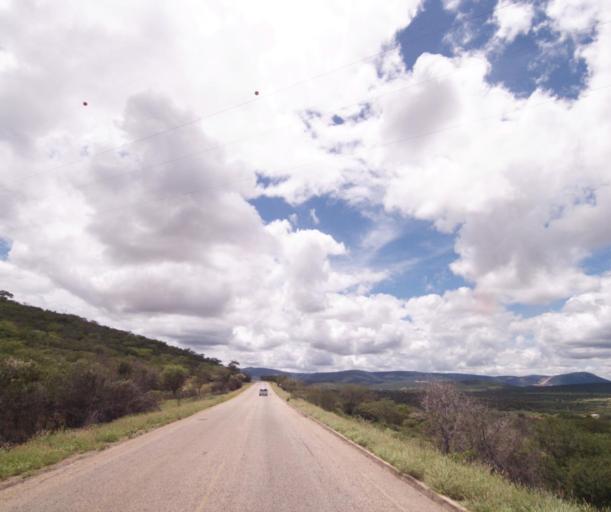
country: BR
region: Bahia
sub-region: Brumado
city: Brumado
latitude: -14.1993
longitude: -41.6106
